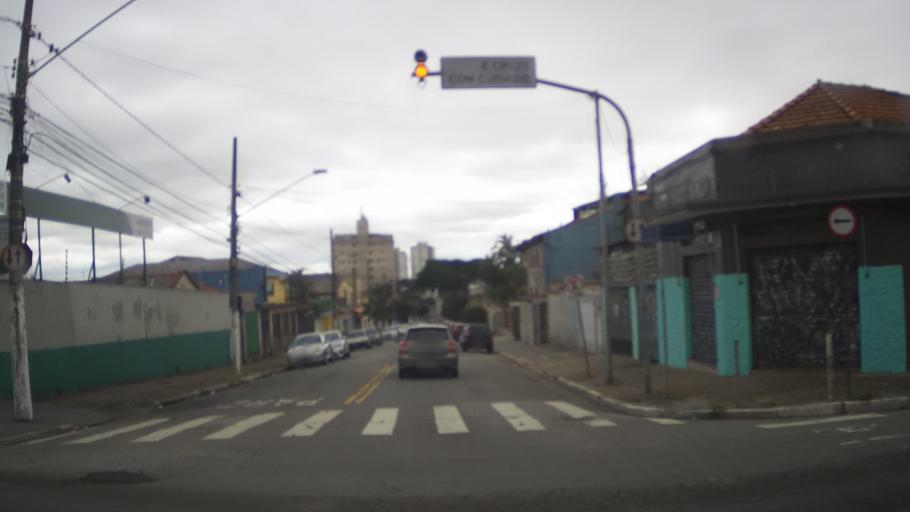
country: BR
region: Sao Paulo
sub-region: Guarulhos
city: Guarulhos
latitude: -23.5216
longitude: -46.5237
